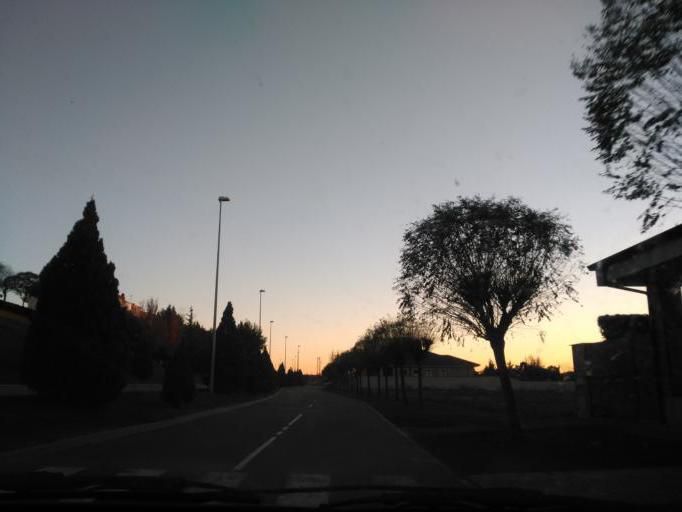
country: ES
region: Castille and Leon
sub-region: Provincia de Salamanca
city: Carbajosa de la Sagrada
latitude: 40.9391
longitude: -5.6489
